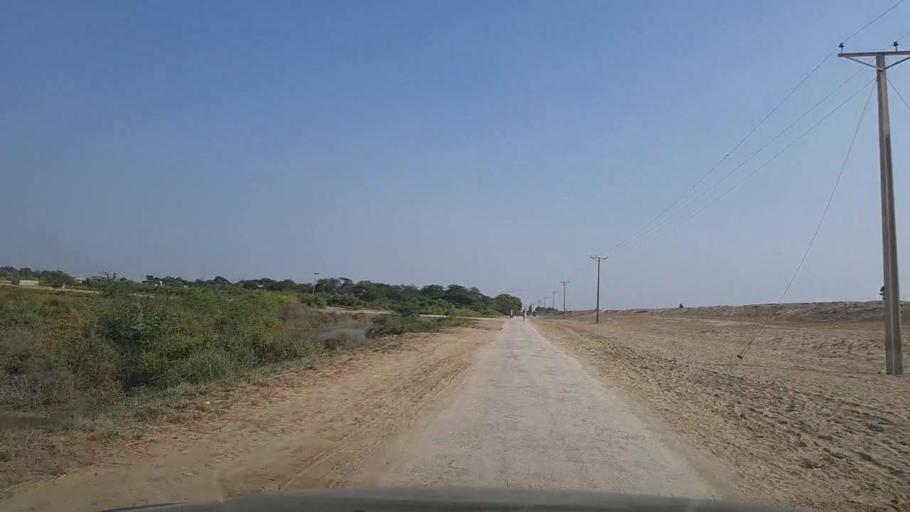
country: PK
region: Sindh
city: Thatta
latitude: 24.5845
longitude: 67.9216
